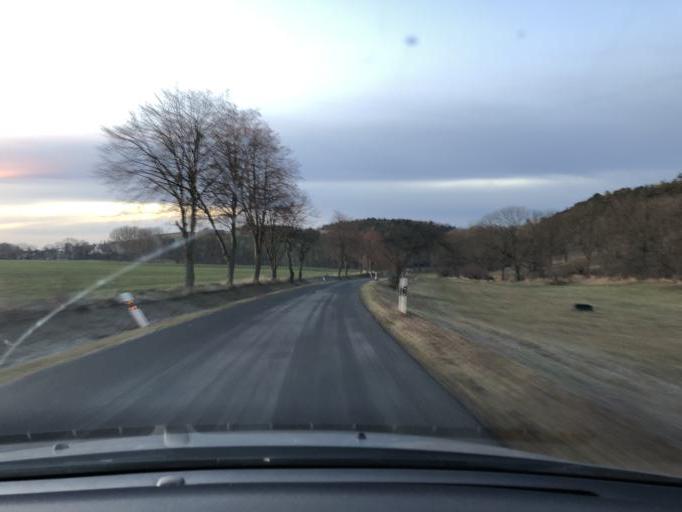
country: DE
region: Thuringia
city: Blankenhain
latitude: 50.8435
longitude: 11.3665
